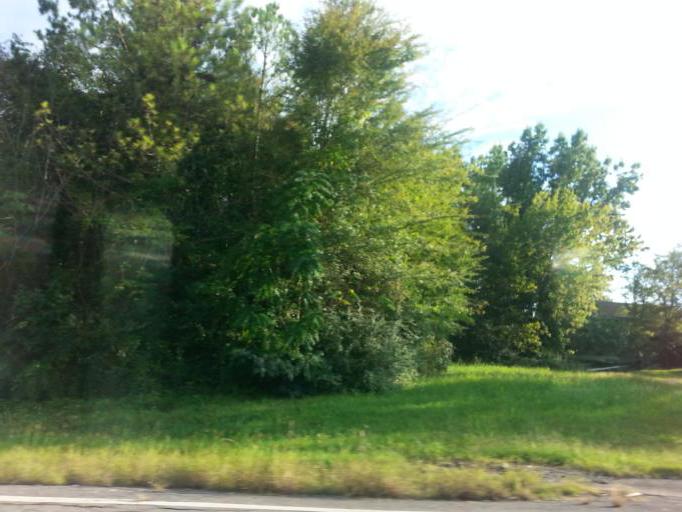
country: US
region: Alabama
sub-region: Lauderdale County
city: Rogersville
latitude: 34.8486
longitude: -87.3903
